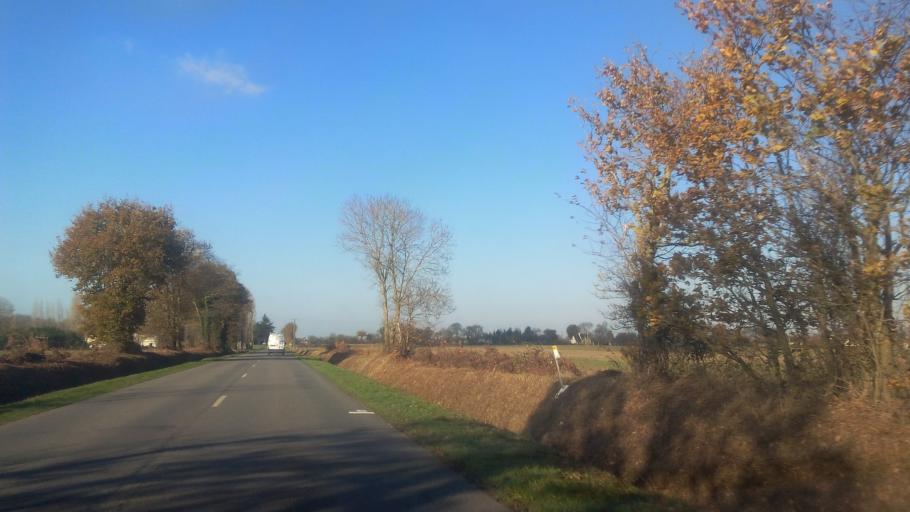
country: FR
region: Brittany
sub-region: Departement du Morbihan
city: Saint-Vincent-sur-Oust
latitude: 47.7048
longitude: -2.1566
